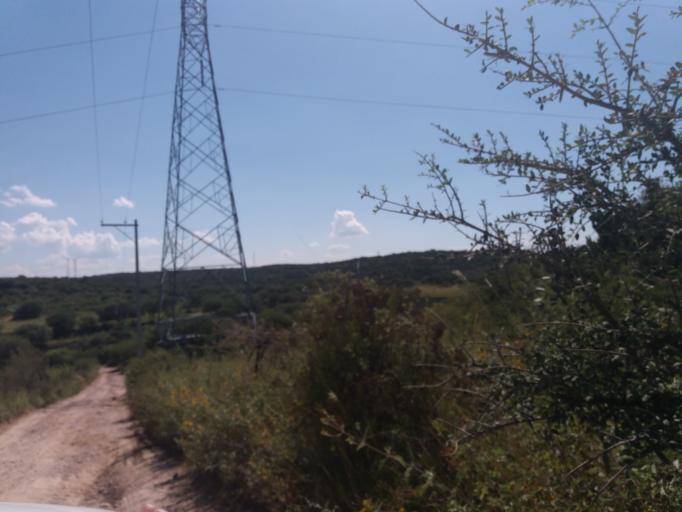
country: MX
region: Aguascalientes
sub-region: Aguascalientes
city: Penuelas (El Cienegal)
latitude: 21.7679
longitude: -102.2387
